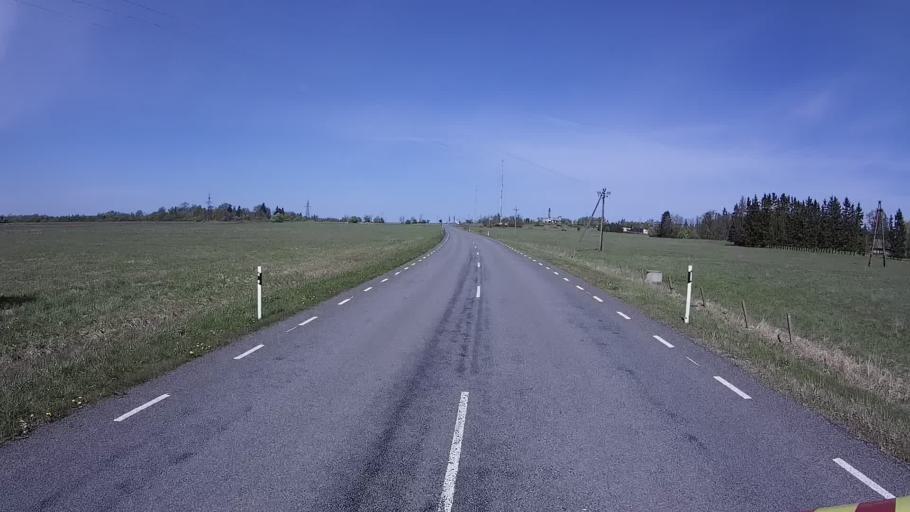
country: EE
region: Laeaene
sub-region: Lihula vald
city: Lihula
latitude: 58.6683
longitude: 23.8315
